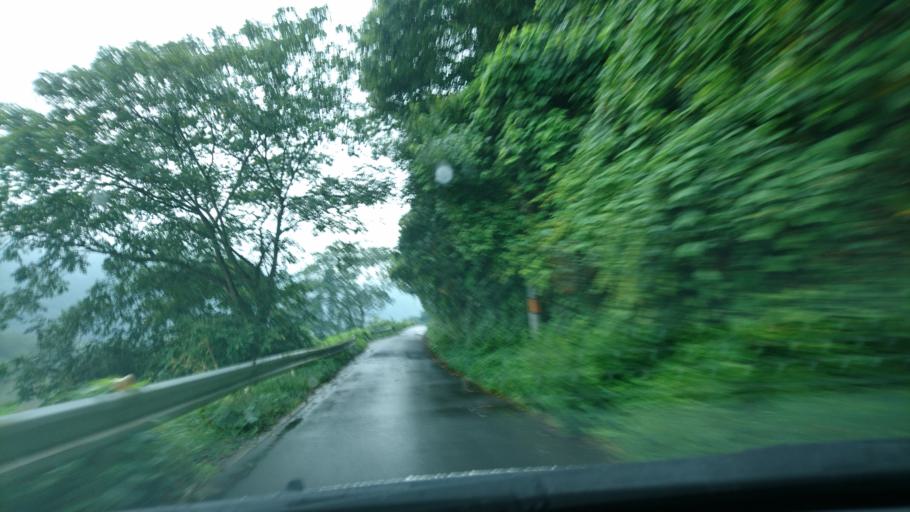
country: JP
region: Iwate
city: Ichinoseki
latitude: 38.8736
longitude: 141.2602
